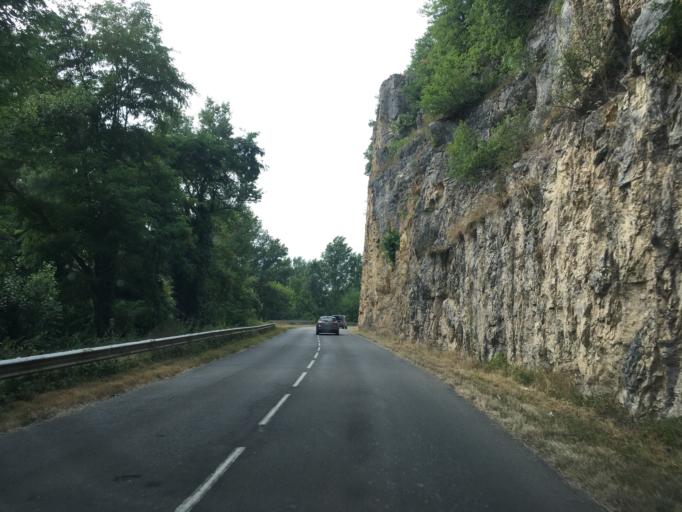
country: FR
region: Midi-Pyrenees
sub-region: Departement du Lot
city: Souillac
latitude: 44.8796
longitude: 1.4909
